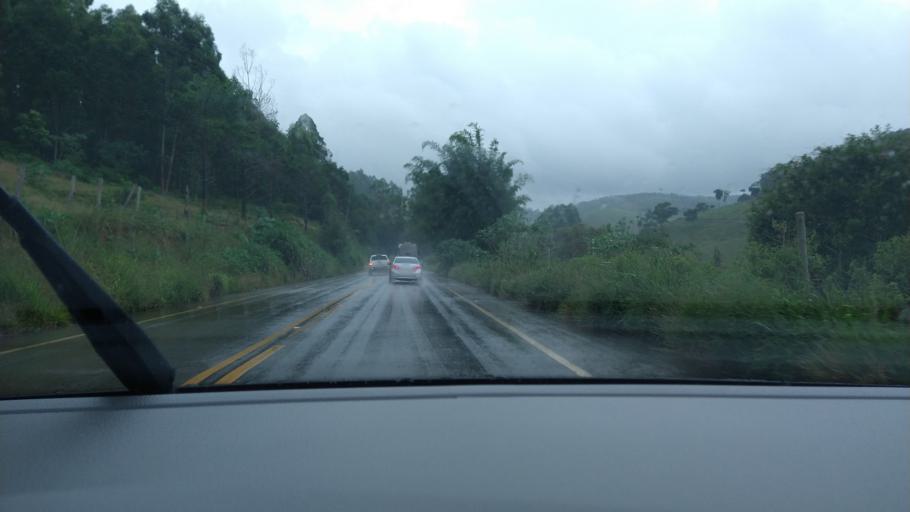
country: BR
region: Minas Gerais
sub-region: Vicosa
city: Vicosa
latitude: -20.6045
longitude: -42.8673
